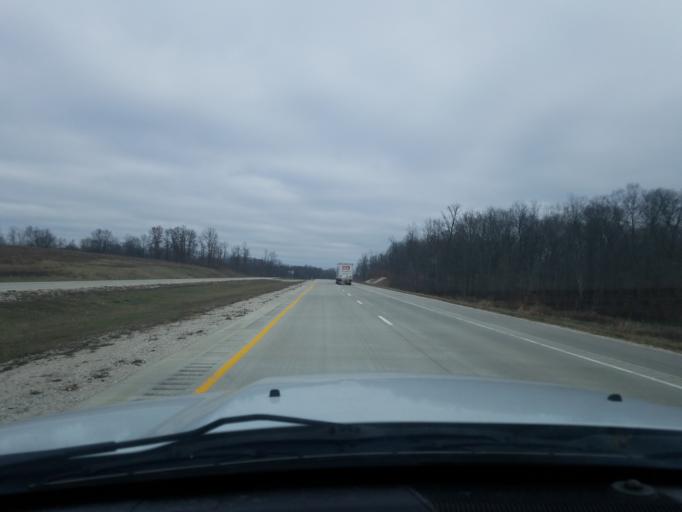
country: US
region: Indiana
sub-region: Greene County
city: Bloomfield
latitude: 38.9462
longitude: -86.8649
